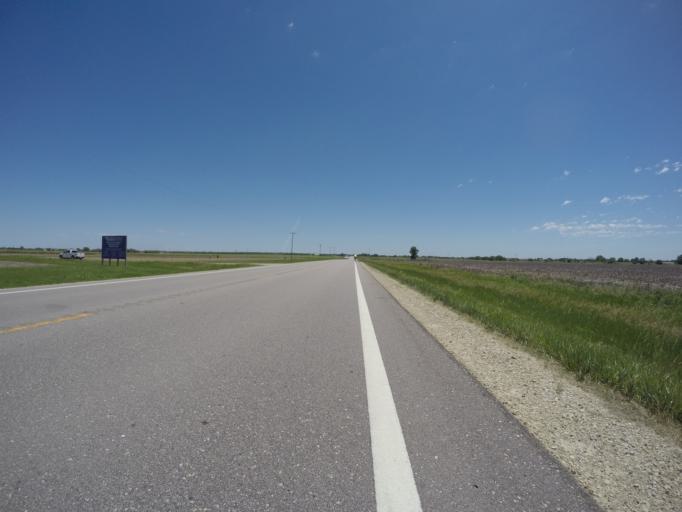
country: US
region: Kansas
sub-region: Republic County
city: Belleville
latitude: 39.8127
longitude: -97.6746
